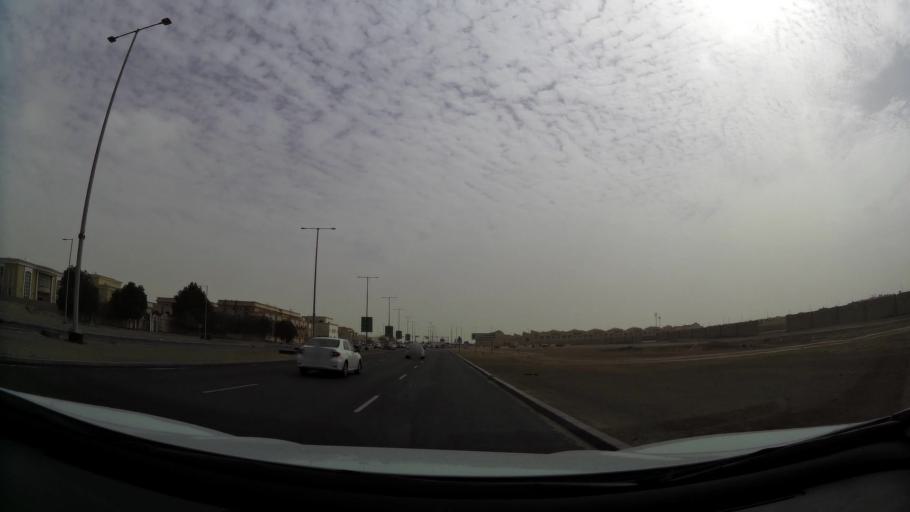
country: AE
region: Abu Dhabi
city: Abu Dhabi
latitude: 24.4061
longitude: 54.5713
